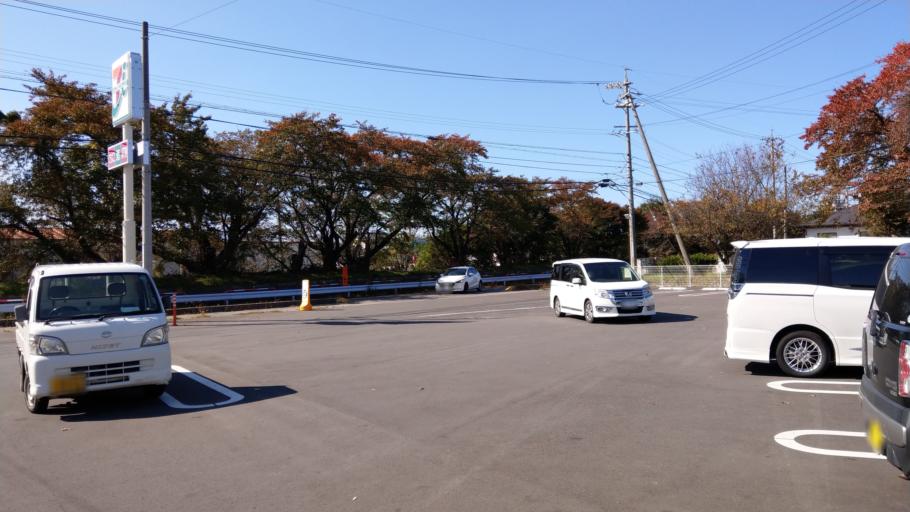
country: JP
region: Nagano
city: Komoro
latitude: 36.3036
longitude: 138.4501
